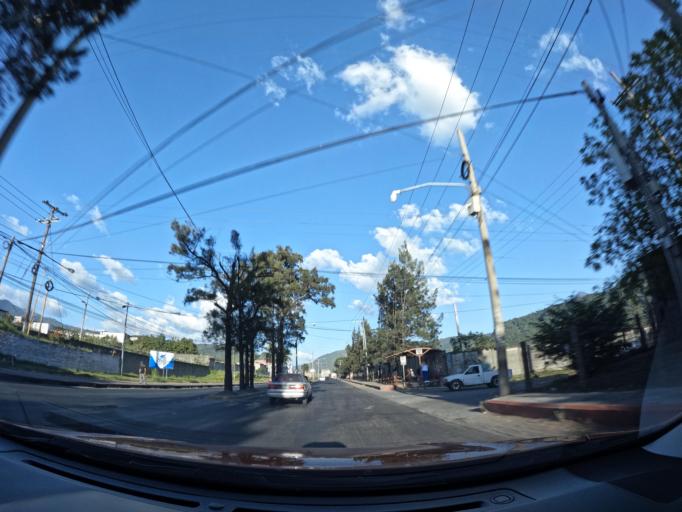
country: GT
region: Escuintla
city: Palin
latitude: 14.4081
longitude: -90.6867
